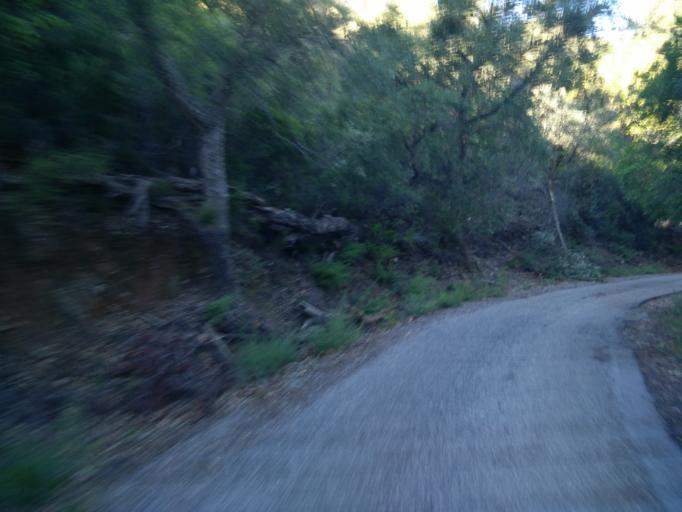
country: FR
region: Provence-Alpes-Cote d'Azur
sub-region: Departement du Var
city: Collobrieres
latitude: 43.2604
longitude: 6.2917
